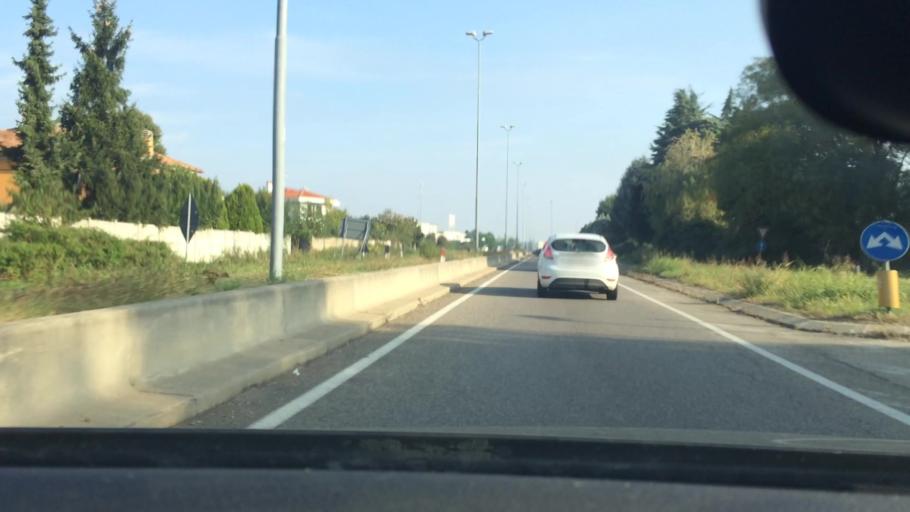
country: IT
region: Lombardy
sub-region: Citta metropolitana di Milano
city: Villa Cortese
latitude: 45.5679
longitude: 8.8983
